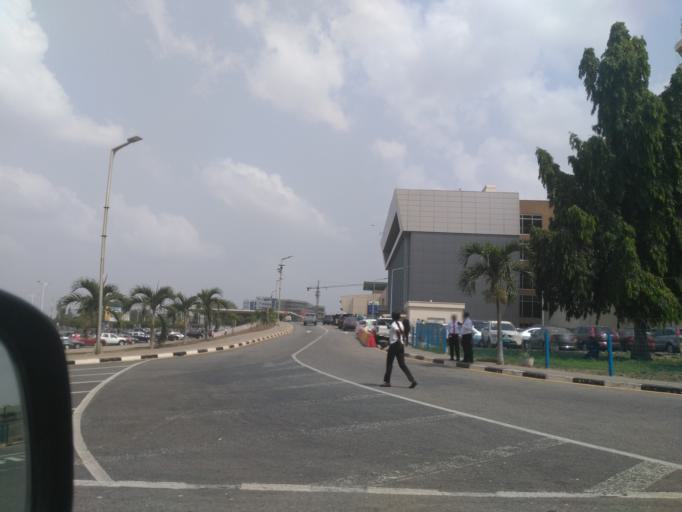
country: GH
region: Greater Accra
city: Accra
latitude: 5.6055
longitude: -0.1724
